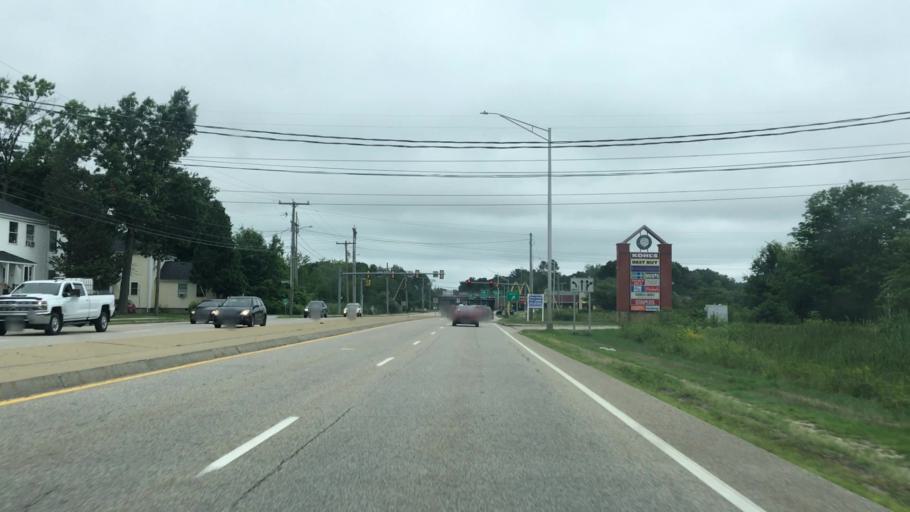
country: US
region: Maine
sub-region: York County
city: South Eliot
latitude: 43.0930
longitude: -70.7971
